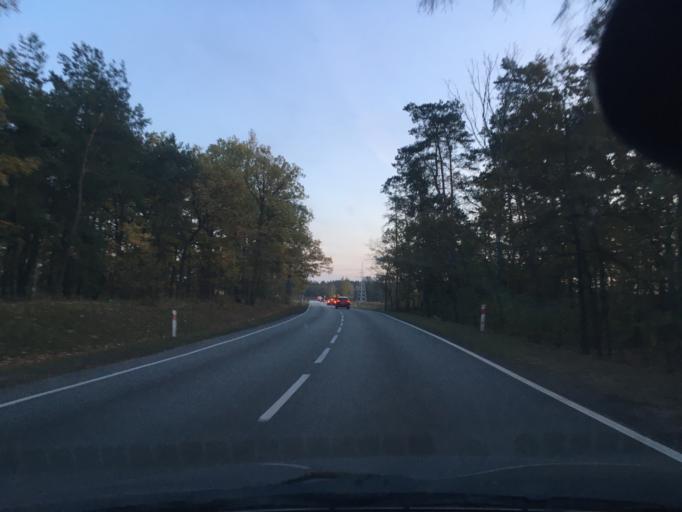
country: PL
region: Masovian Voivodeship
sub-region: Powiat sochaczewski
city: Mlodzieszyn
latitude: 52.3369
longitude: 20.2149
